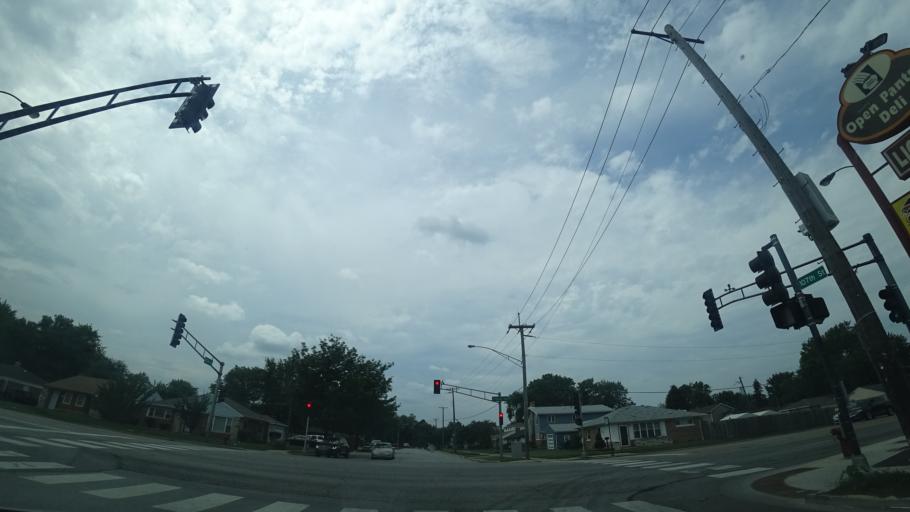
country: US
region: Illinois
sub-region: Cook County
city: Merrionette Park
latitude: 41.6986
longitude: -87.7203
